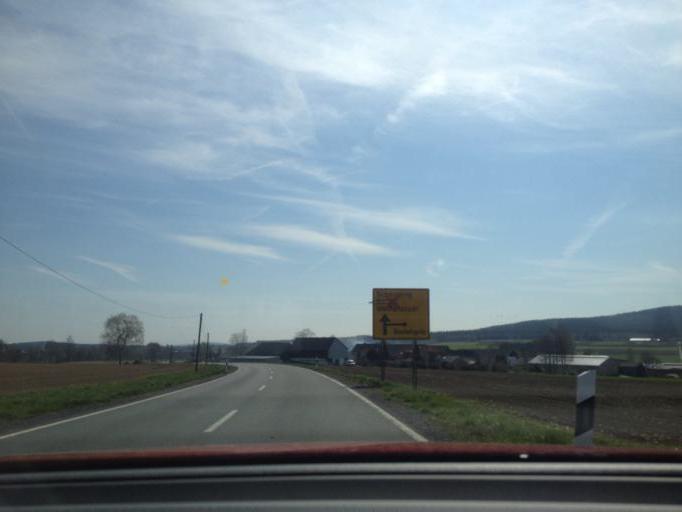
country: DE
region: Bavaria
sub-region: Upper Franconia
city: Zell im Fichtelgebirge
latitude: 50.0955
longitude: 11.8422
